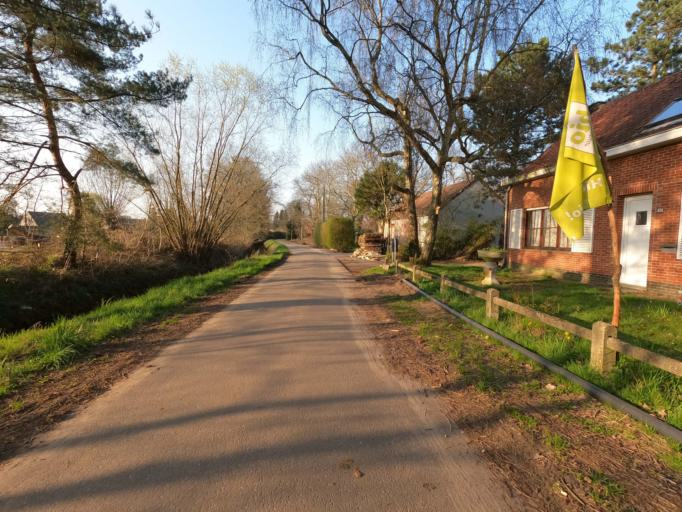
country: BE
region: Flanders
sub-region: Provincie Antwerpen
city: Hulshout
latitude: 51.0489
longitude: 4.7834
